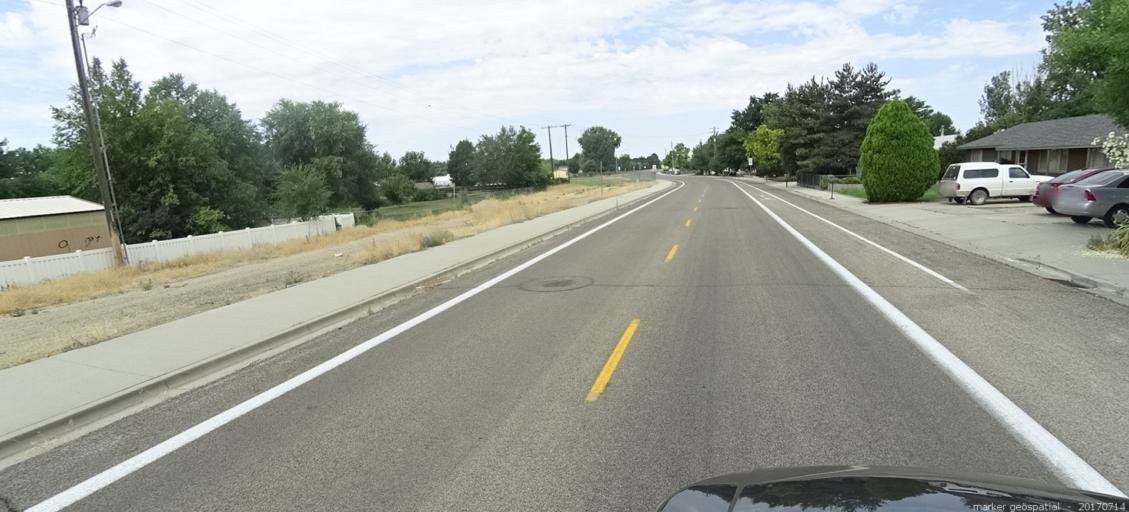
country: US
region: Idaho
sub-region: Ada County
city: Kuna
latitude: 43.4959
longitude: -116.4199
